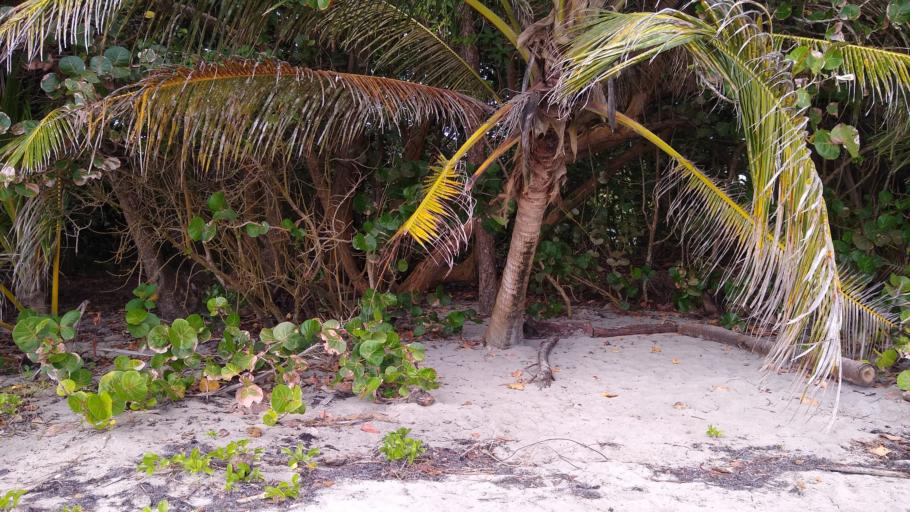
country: MQ
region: Martinique
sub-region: Martinique
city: Les Trois-Ilets
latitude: 14.4745
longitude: -61.0390
